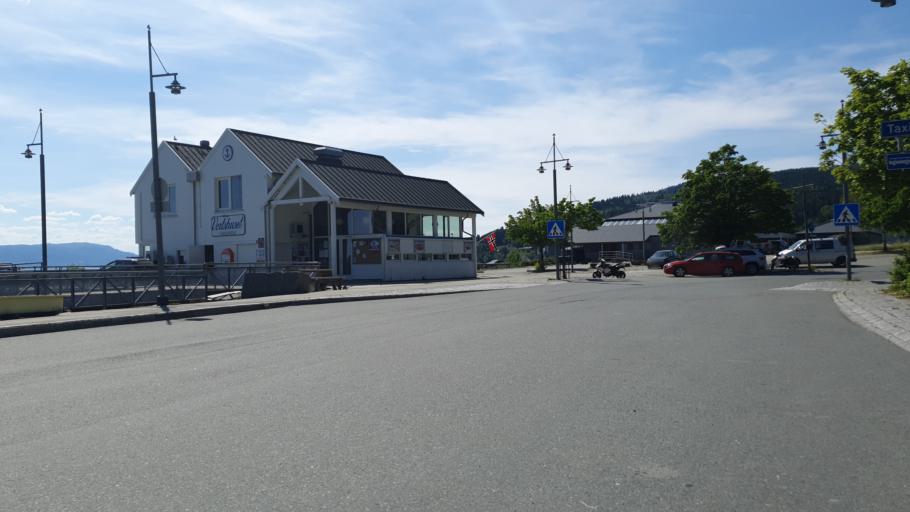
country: NO
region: Sor-Trondelag
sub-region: Trondheim
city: Trondheim
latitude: 63.5535
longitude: 10.2231
